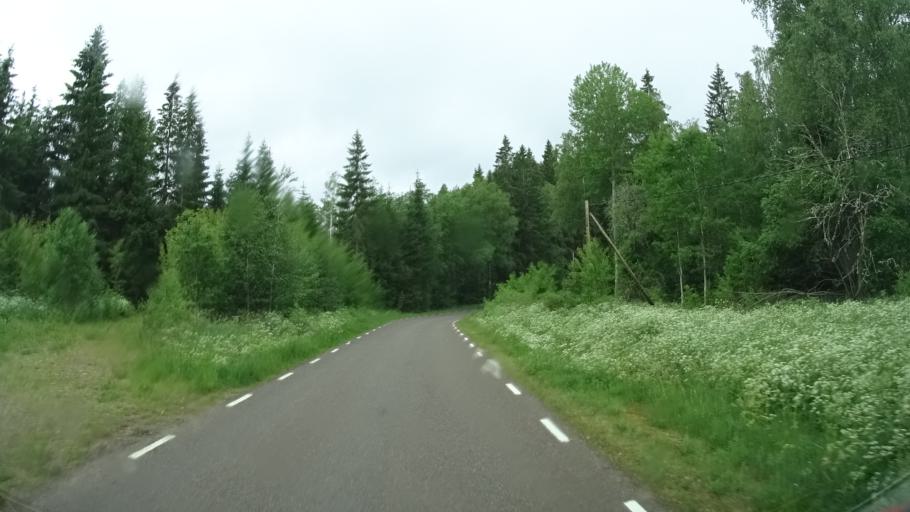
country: SE
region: Kalmar
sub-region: Vimmerby Kommun
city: Sodra Vi
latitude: 57.7085
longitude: 15.7630
